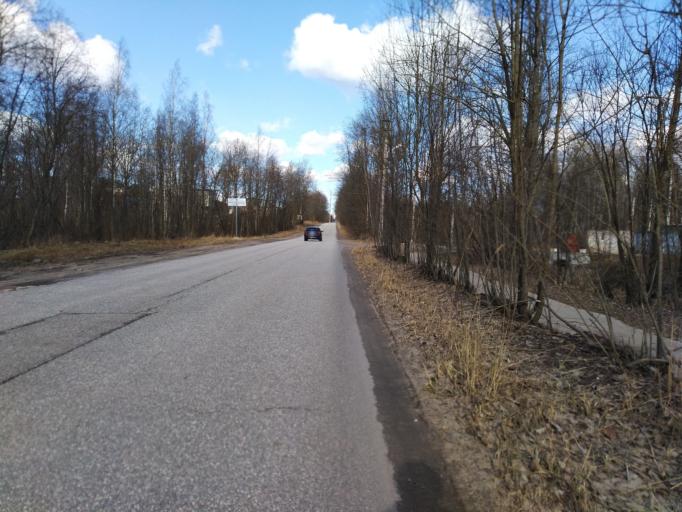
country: RU
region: Leningrad
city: Novoye Devyatkino
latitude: 60.1008
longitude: 30.4783
